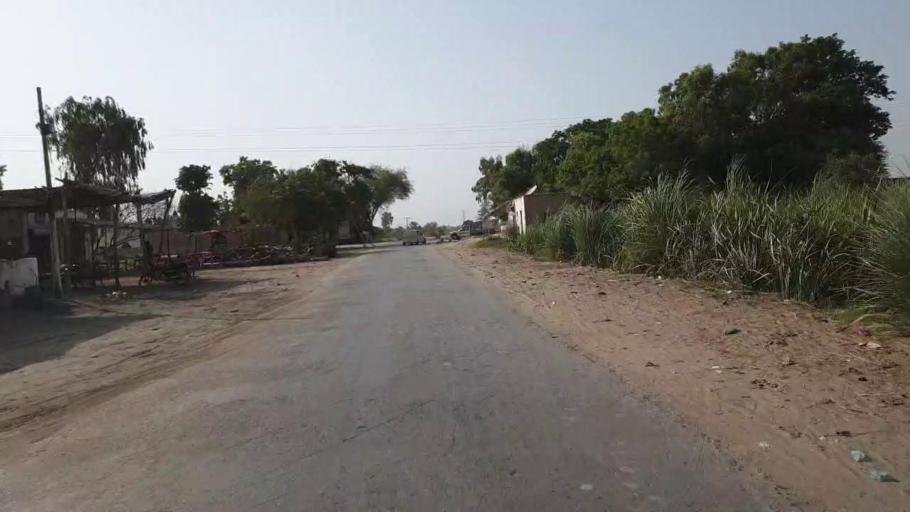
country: PK
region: Sindh
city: Sanghar
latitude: 26.2633
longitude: 68.9301
